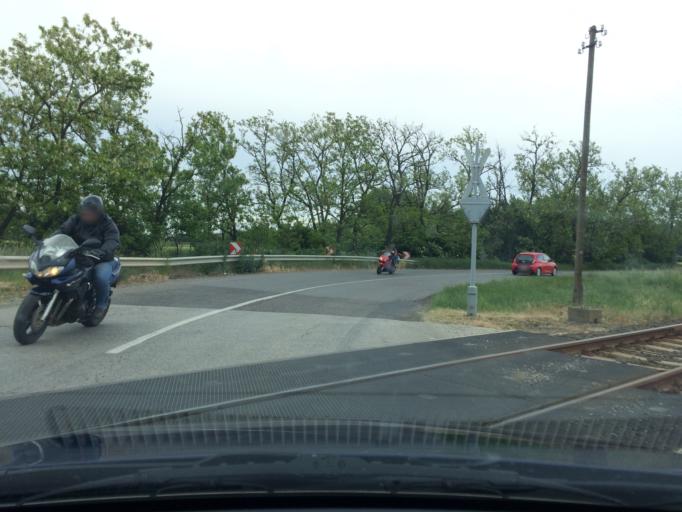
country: HU
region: Szabolcs-Szatmar-Bereg
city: Tiszavasvari
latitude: 47.9205
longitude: 21.3934
